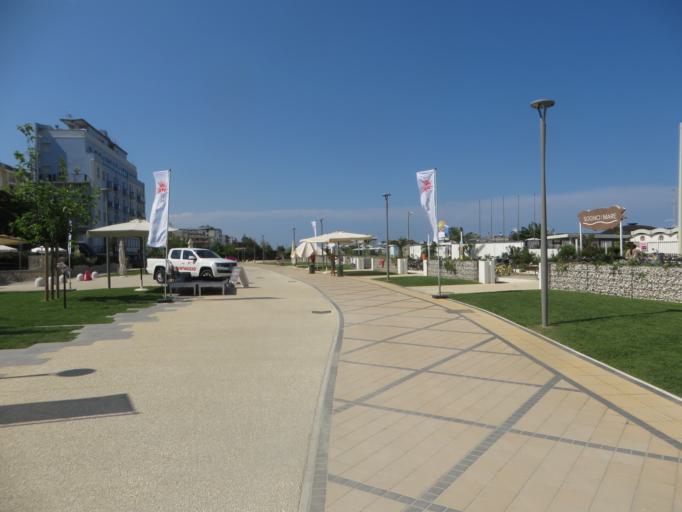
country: IT
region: Emilia-Romagna
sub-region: Provincia di Ravenna
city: Cervia
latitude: 44.2779
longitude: 12.3528
